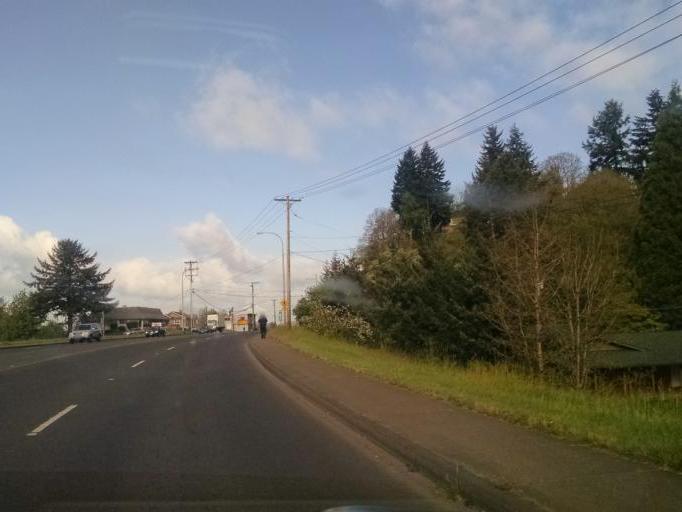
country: US
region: Washington
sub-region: Cowlitz County
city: Kelso
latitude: 46.1436
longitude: -122.9020
